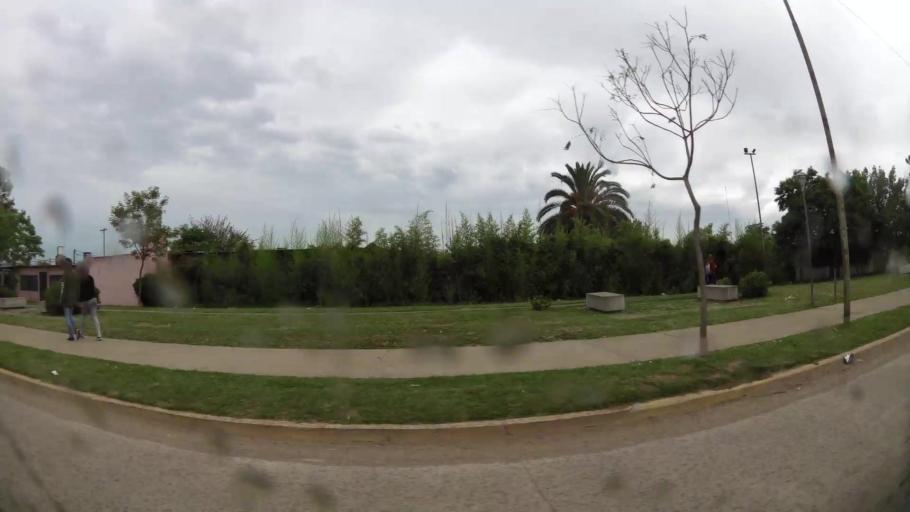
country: AR
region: Buenos Aires
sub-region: Partido de Zarate
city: Zarate
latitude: -34.1101
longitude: -59.0333
